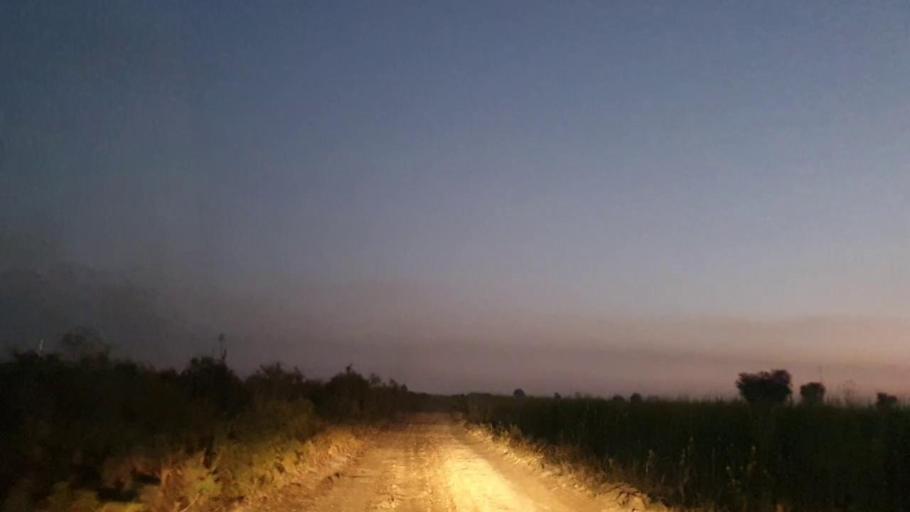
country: PK
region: Sindh
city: Nawabshah
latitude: 26.3285
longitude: 68.3761
